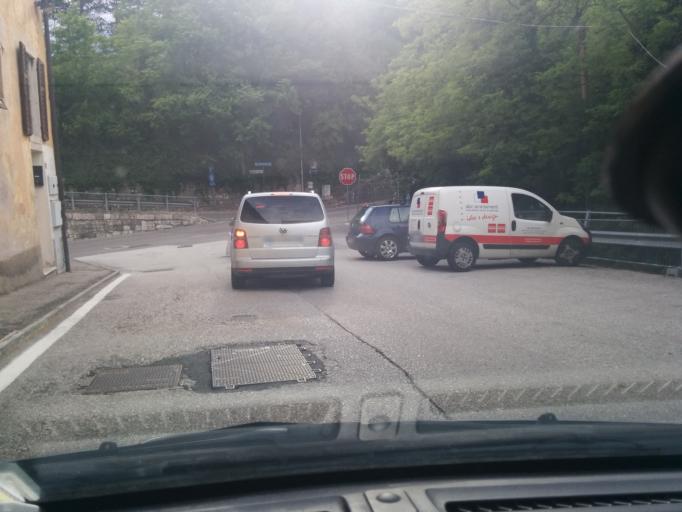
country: IT
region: Trentino-Alto Adige
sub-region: Provincia di Trento
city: Povo
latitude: 46.0739
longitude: 11.1509
